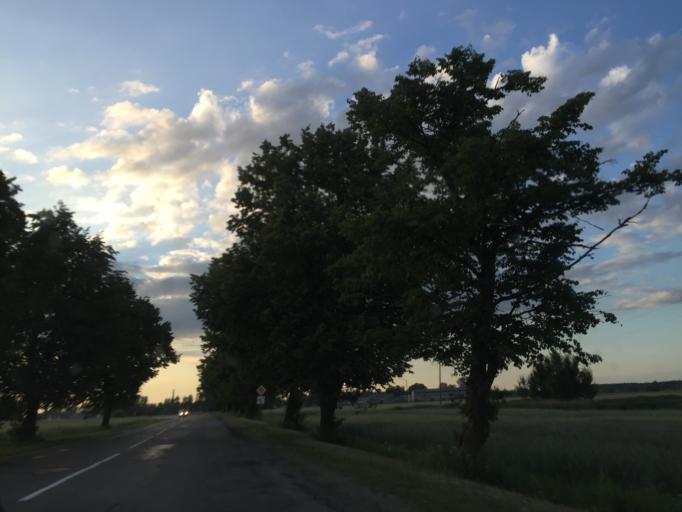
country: LV
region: Sigulda
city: Sigulda
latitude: 57.1353
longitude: 24.8950
